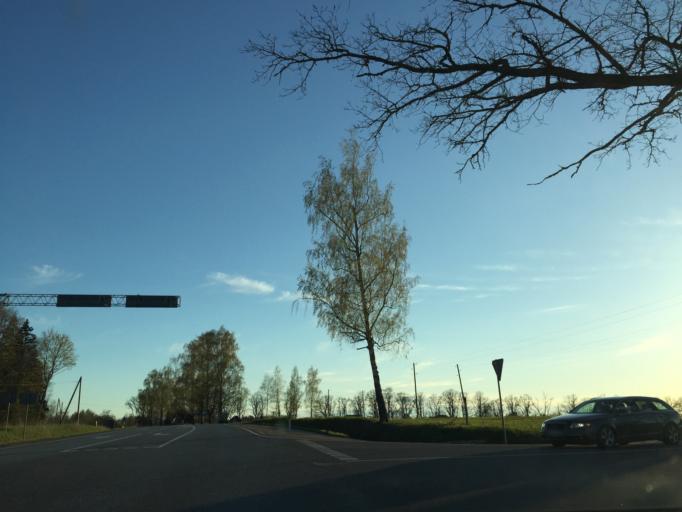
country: LV
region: Koceni
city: Koceni
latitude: 57.5171
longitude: 25.3496
